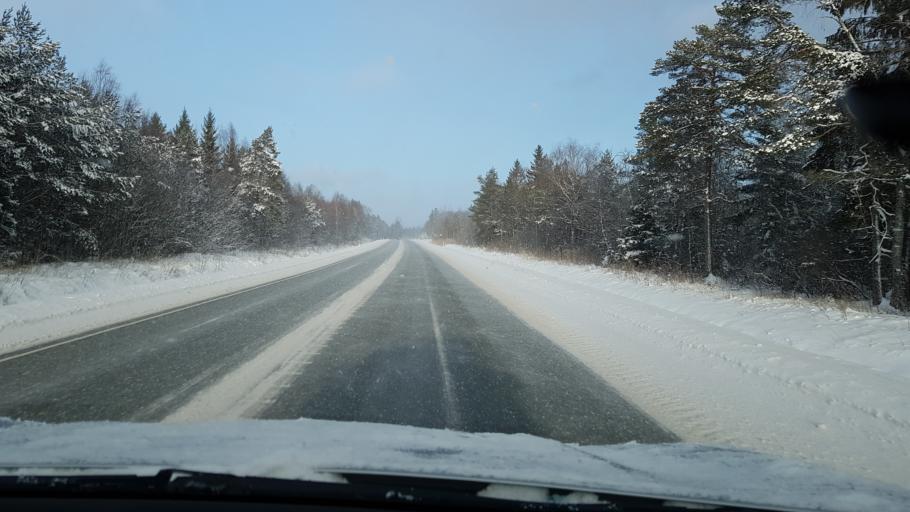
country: EE
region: Harju
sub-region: Nissi vald
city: Riisipere
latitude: 59.1528
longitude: 24.3394
